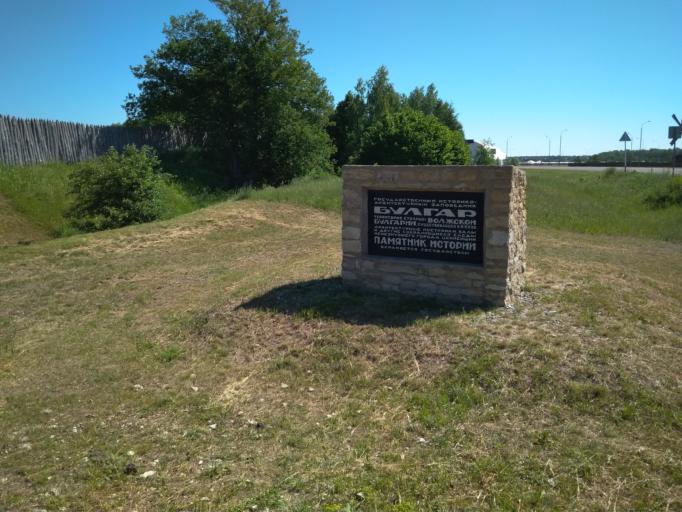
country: RU
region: Tatarstan
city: Bolgar
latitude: 54.9679
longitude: 49.0605
